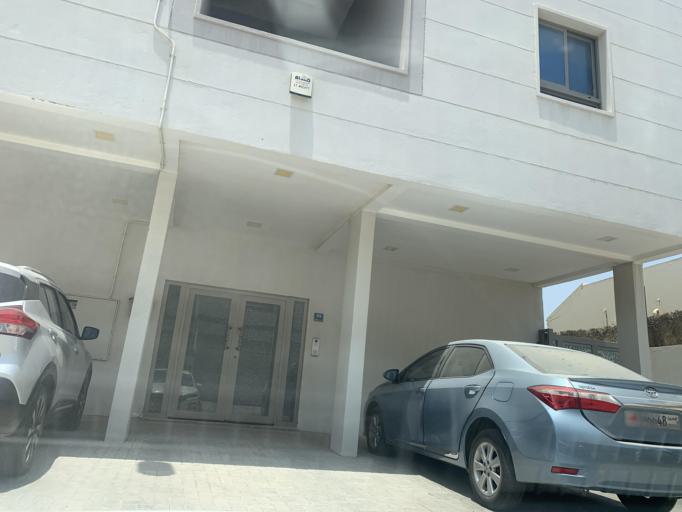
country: BH
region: Manama
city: Jidd Hafs
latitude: 26.2122
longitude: 50.4731
